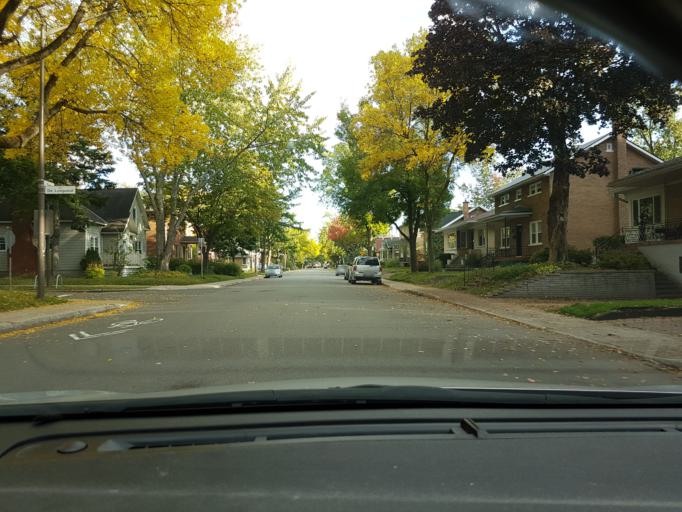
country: CA
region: Quebec
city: Quebec
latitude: 46.7915
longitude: -71.2562
